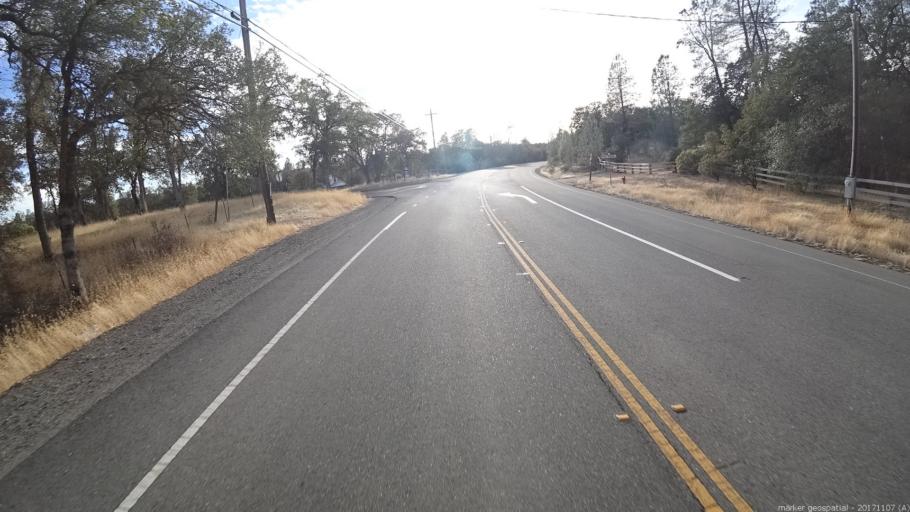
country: US
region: California
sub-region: Shasta County
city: Shasta
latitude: 40.5195
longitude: -122.4800
